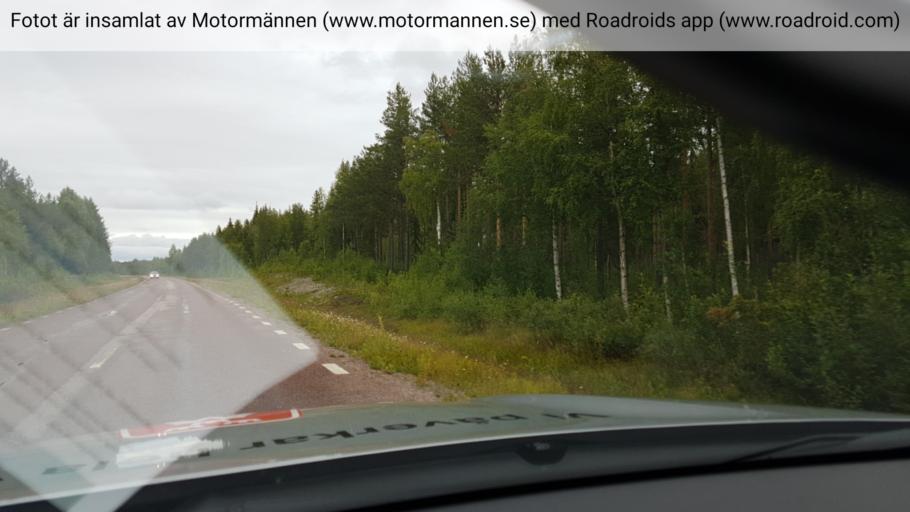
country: SE
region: Norrbotten
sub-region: Pajala Kommun
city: Pajala
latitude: 67.1448
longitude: 22.6206
